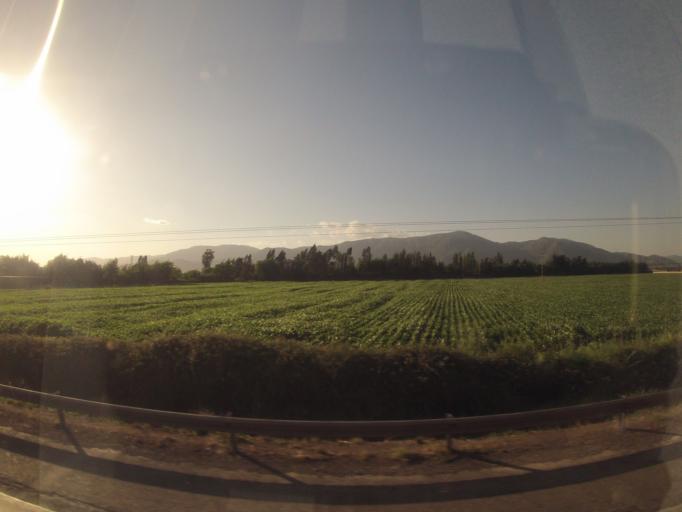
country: CL
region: O'Higgins
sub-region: Provincia de Colchagua
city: Chimbarongo
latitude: -34.5881
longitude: -70.9672
